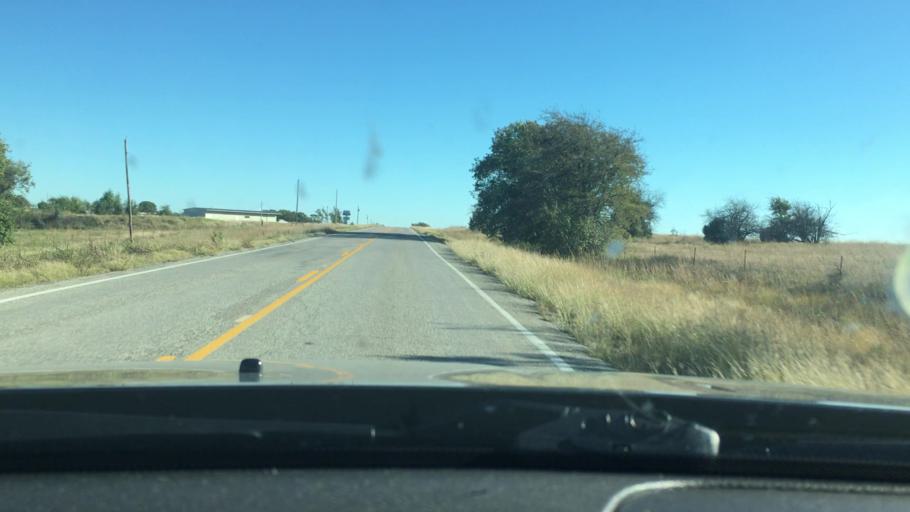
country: US
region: Oklahoma
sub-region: Marshall County
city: Madill
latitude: 34.1296
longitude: -96.7224
